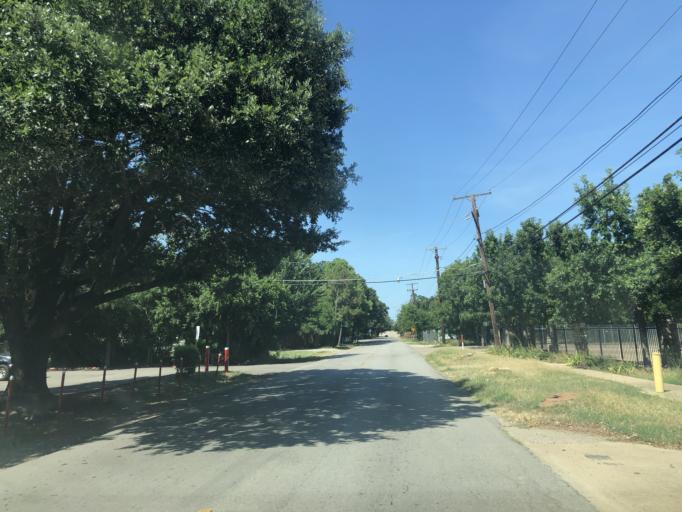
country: US
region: Texas
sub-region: Dallas County
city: University Park
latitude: 32.8291
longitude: -96.8511
